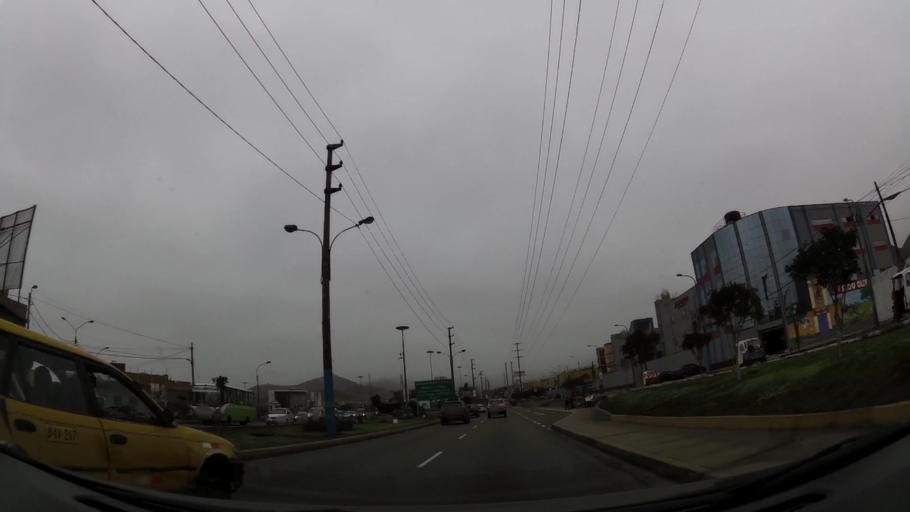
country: PE
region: Lima
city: Ventanilla
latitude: -11.8796
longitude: -77.1264
